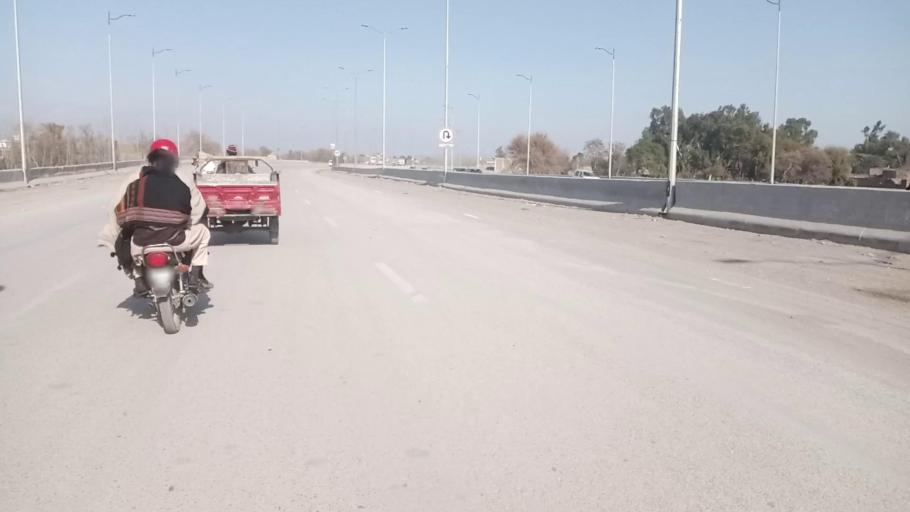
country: PK
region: Khyber Pakhtunkhwa
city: Peshawar
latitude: 34.0380
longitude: 71.5334
